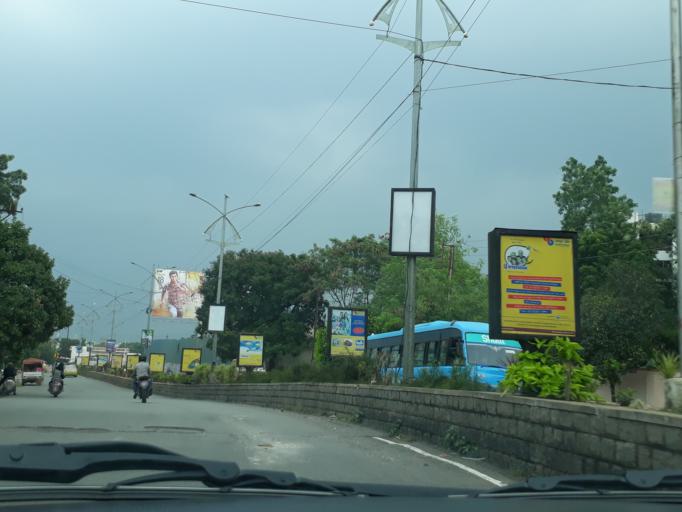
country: IN
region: Telangana
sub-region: Rangareddi
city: Kukatpalli
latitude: 17.4319
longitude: 78.4189
